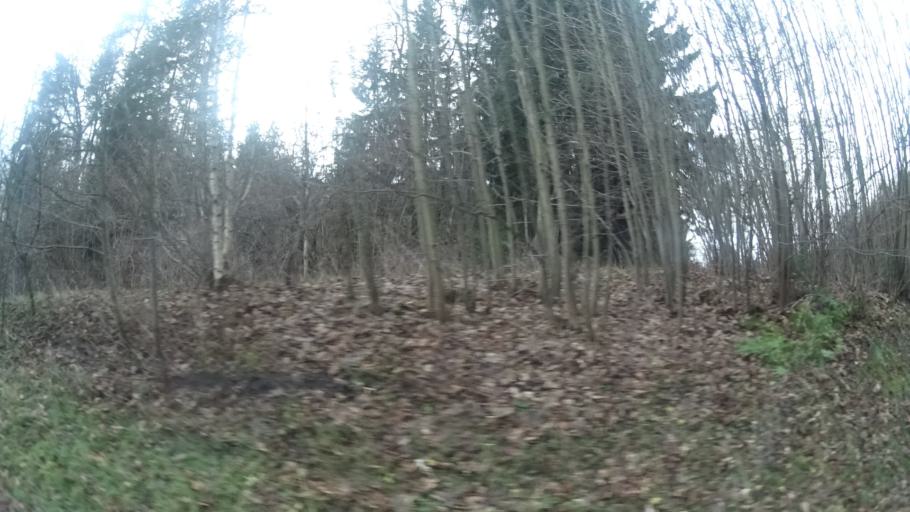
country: DE
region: Thuringia
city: Wittgendorf
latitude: 50.5933
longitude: 11.2291
